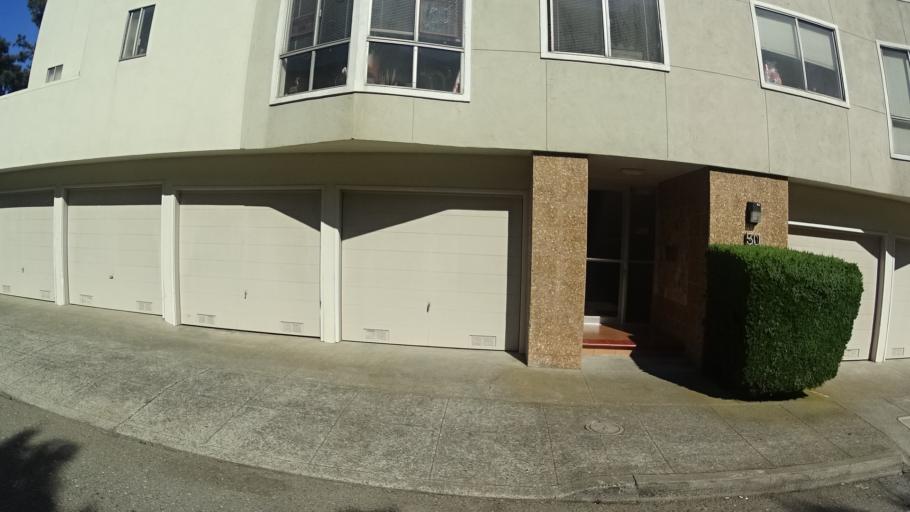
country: US
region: California
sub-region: San Francisco County
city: San Francisco
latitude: 37.7523
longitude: -122.4453
